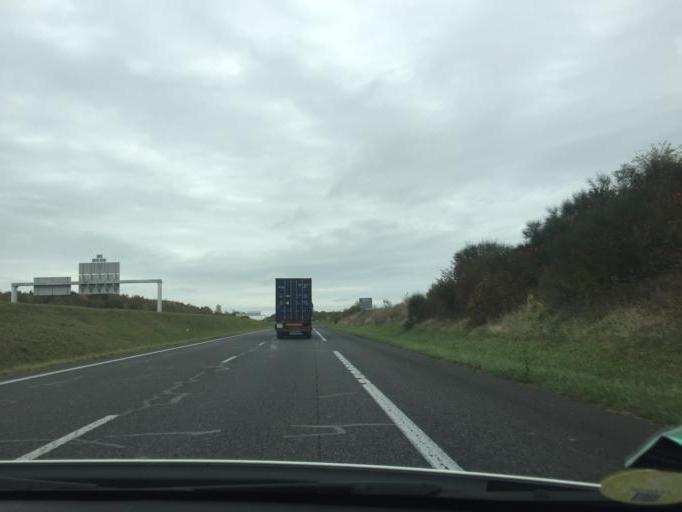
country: FR
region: Centre
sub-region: Departement du Loiret
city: Courtenay
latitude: 48.0707
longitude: 3.1158
